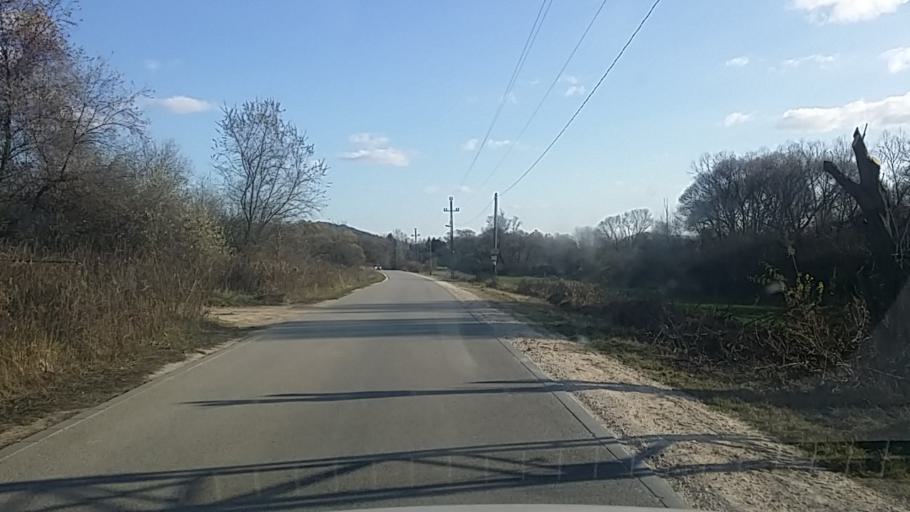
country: HU
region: Pest
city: Pilisszanto
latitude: 47.6506
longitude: 18.9038
